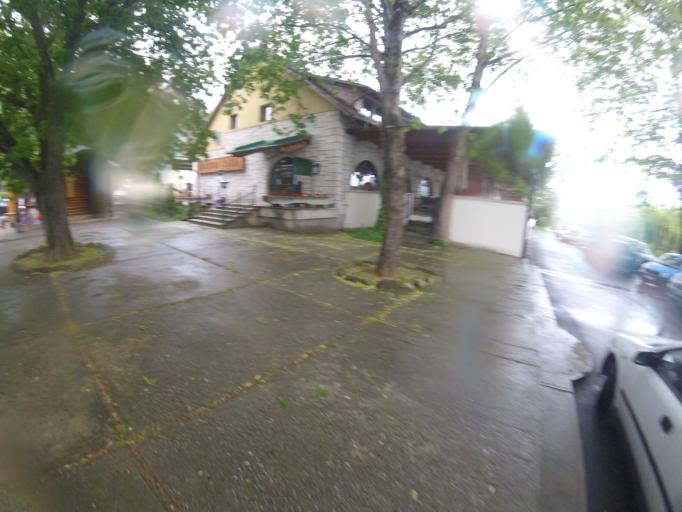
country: HU
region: Borsod-Abauj-Zemplen
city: Tokaj
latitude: 48.1200
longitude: 21.4130
